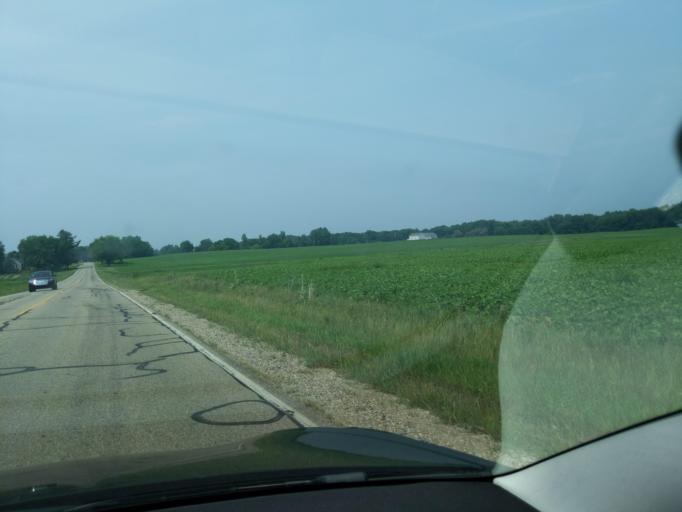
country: US
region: Michigan
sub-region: Clinton County
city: DeWitt
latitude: 42.7930
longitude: -84.5692
